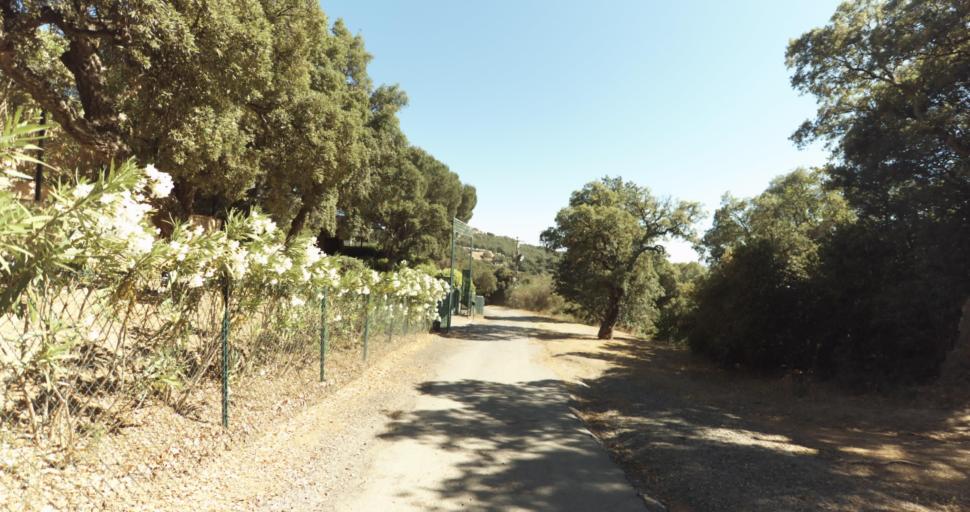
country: FR
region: Provence-Alpes-Cote d'Azur
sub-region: Departement du Var
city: Gassin
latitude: 43.2371
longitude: 6.5843
